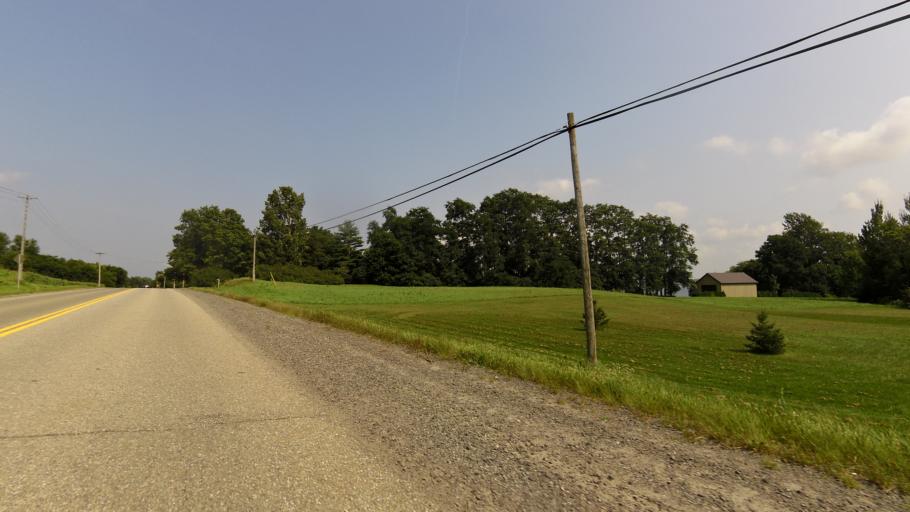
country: CA
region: Ontario
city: Prescott
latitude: 44.6820
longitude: -75.5574
